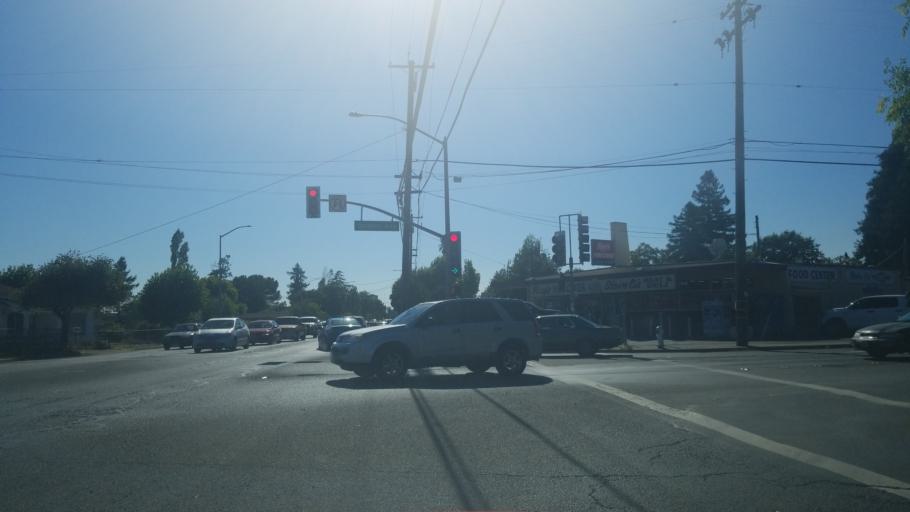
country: US
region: California
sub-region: Sonoma County
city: Roseland
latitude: 38.4144
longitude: -122.7233
